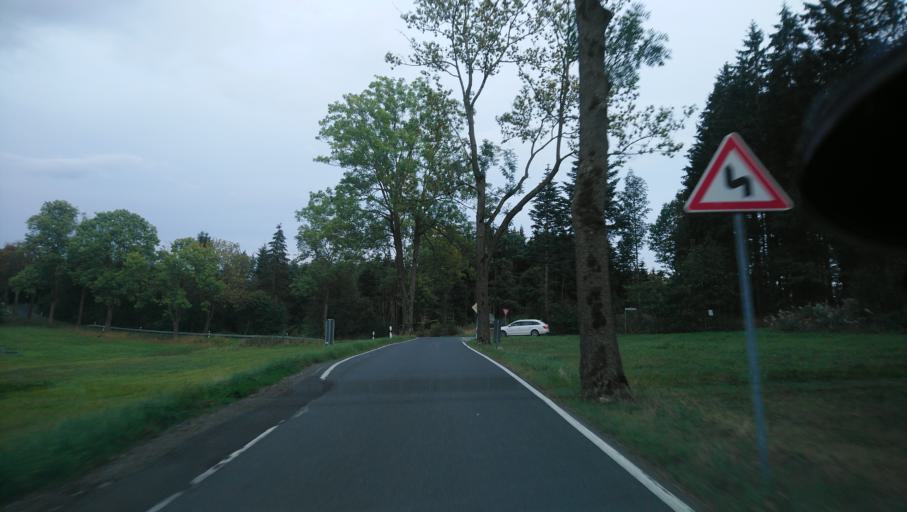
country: DE
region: Saxony
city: Barenstein
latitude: 50.5274
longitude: 13.0177
